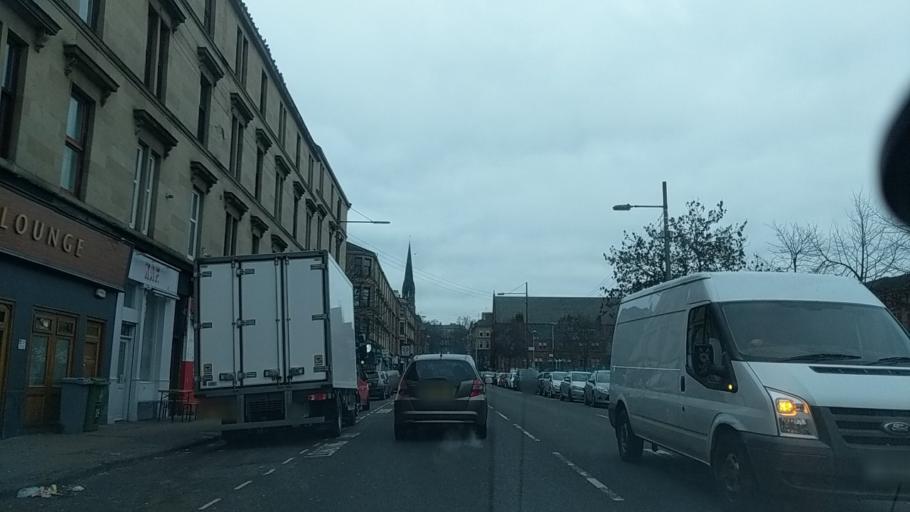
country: GB
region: Scotland
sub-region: Glasgow City
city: Glasgow
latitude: 55.8709
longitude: -4.3028
